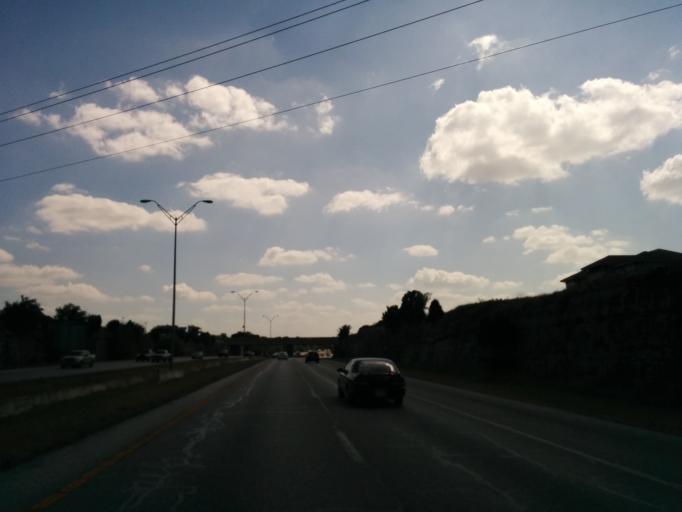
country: US
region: Texas
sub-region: Bexar County
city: Shavano Park
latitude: 29.6047
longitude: -98.5312
